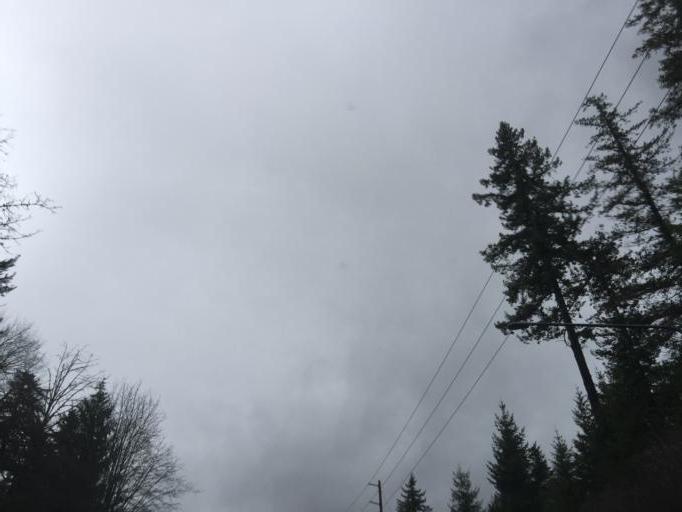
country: US
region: Washington
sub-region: King County
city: Snoqualmie
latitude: 47.5169
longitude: -121.8414
